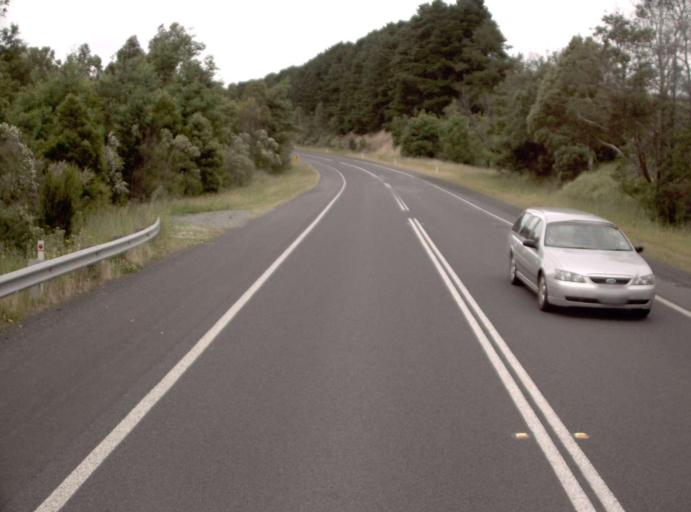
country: AU
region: Victoria
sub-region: Bass Coast
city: North Wonthaggi
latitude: -38.3759
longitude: 145.7216
